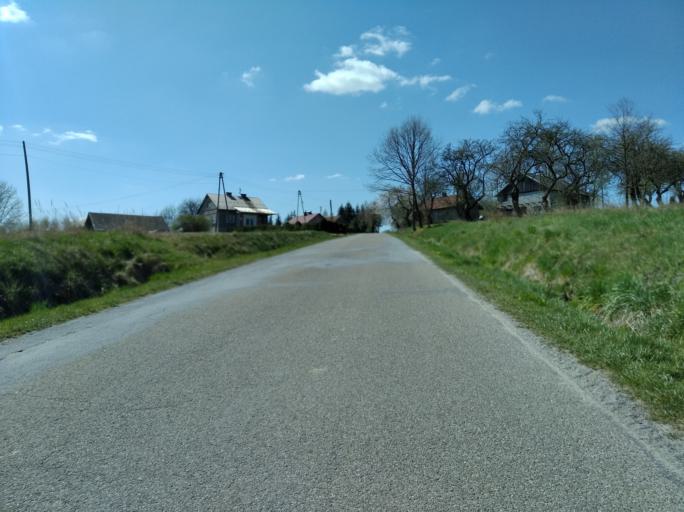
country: PL
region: Subcarpathian Voivodeship
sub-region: Powiat strzyzowski
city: Wisniowa
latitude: 49.9059
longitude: 21.6743
